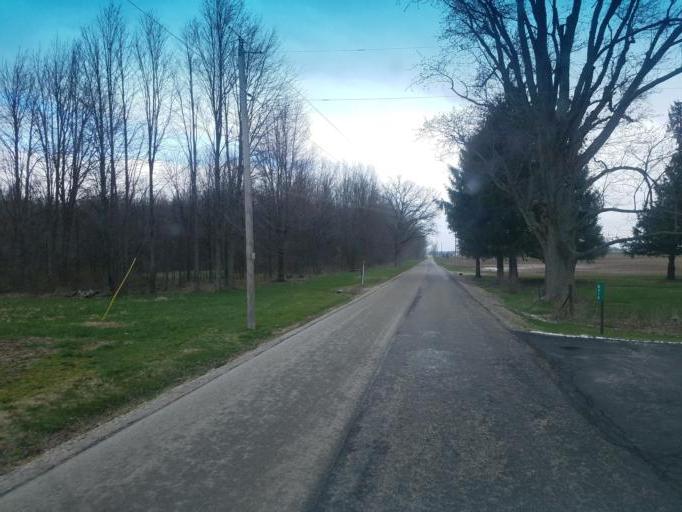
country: US
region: Ohio
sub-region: Marion County
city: Prospect
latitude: 40.4338
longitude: -83.1139
